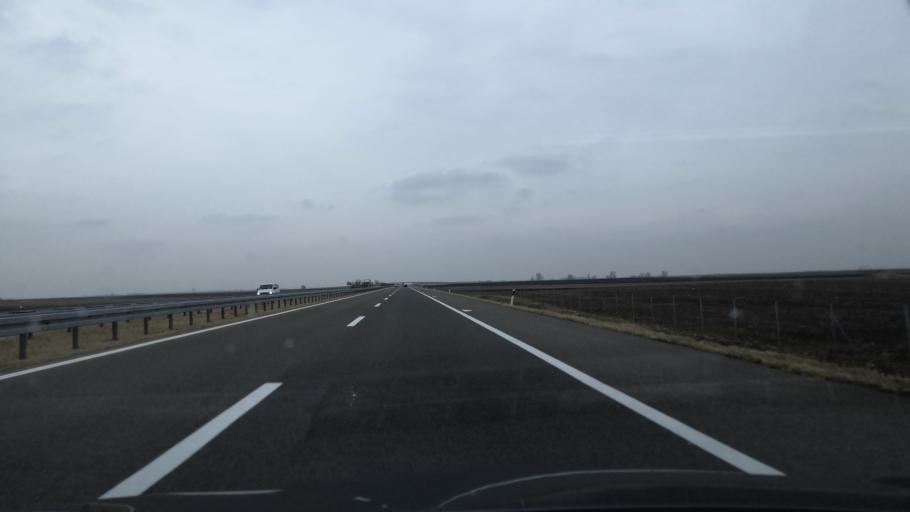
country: RS
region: Autonomna Pokrajina Vojvodina
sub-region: Severnobacki Okrug
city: Backa Topola
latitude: 45.8784
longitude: 19.7001
